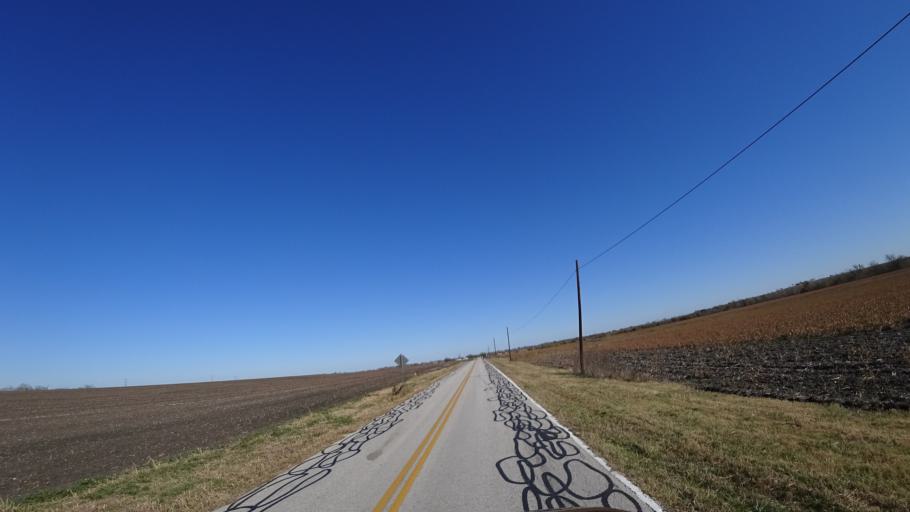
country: US
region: Texas
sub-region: Travis County
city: Garfield
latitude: 30.1014
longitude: -97.6562
